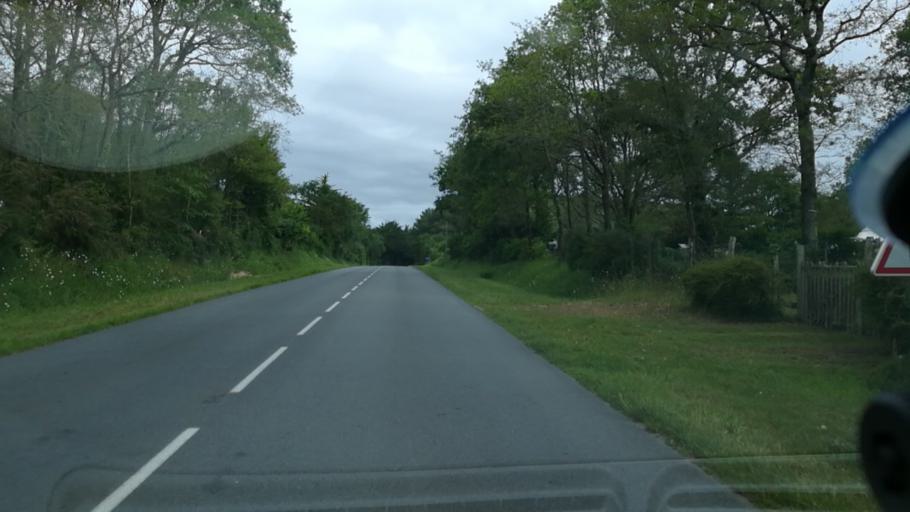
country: FR
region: Brittany
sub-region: Departement du Morbihan
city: Penestin
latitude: 47.4659
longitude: -2.4786
